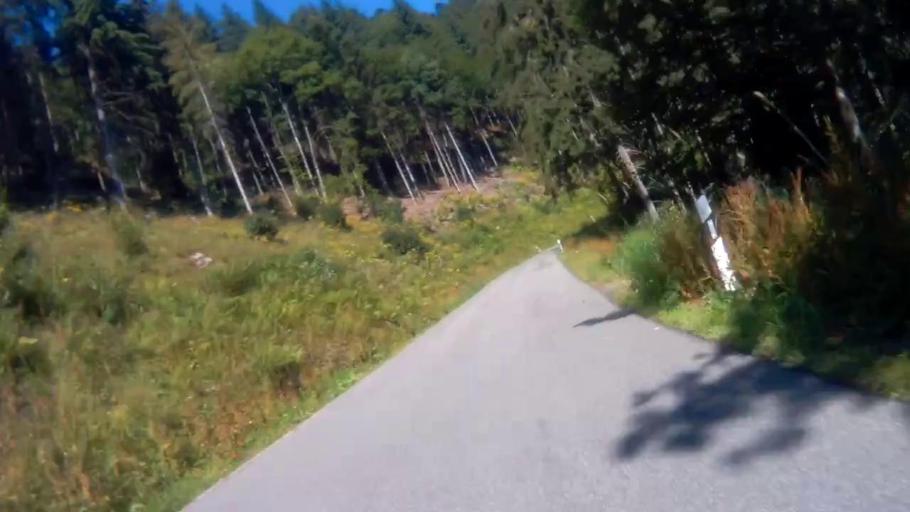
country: DE
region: Baden-Wuerttemberg
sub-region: Freiburg Region
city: Badenweiler
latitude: 47.7855
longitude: 7.7083
